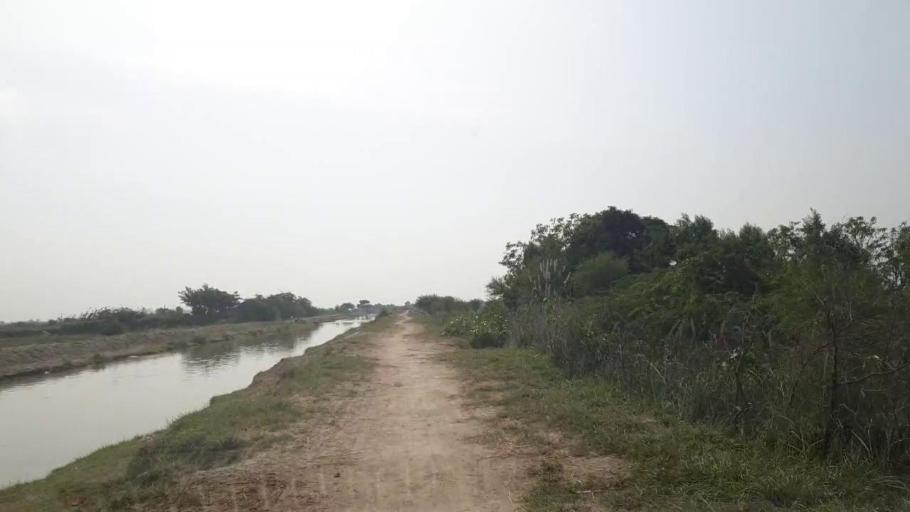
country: PK
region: Sindh
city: Badin
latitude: 24.5599
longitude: 68.8497
